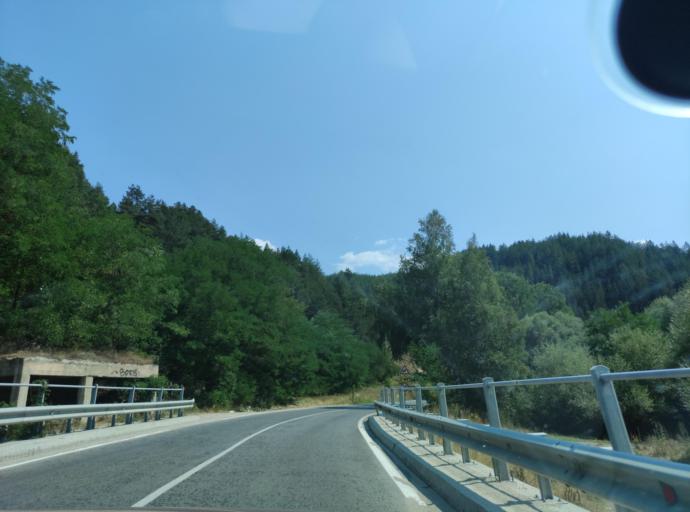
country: BG
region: Blagoevgrad
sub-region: Obshtina Belitsa
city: Belitsa
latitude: 41.8952
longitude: 23.5404
